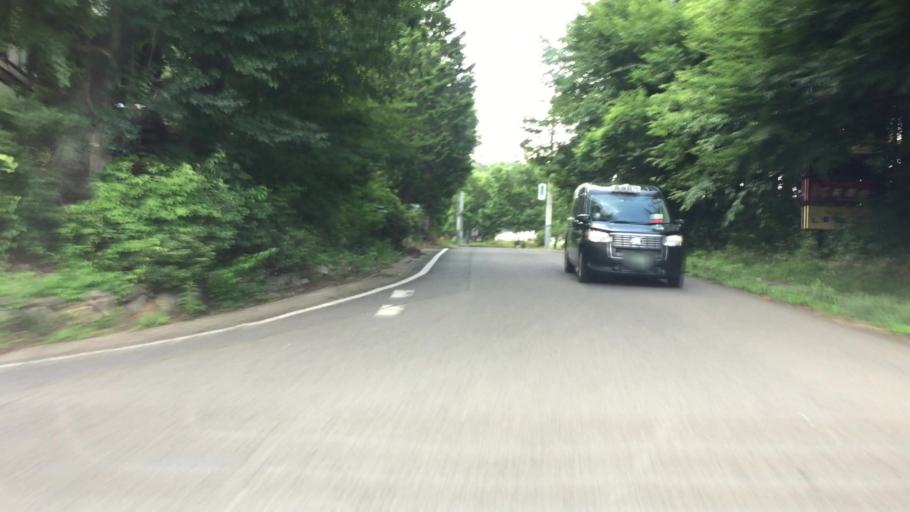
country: JP
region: Tochigi
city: Kuroiso
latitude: 37.0363
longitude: 140.0267
